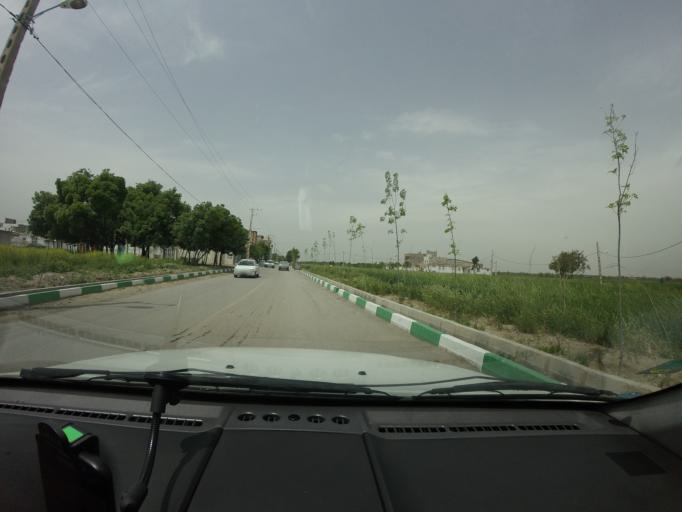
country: IR
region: Tehran
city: Shahrak-e Emam Hasan-e Mojtaba
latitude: 35.5325
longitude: 51.3319
